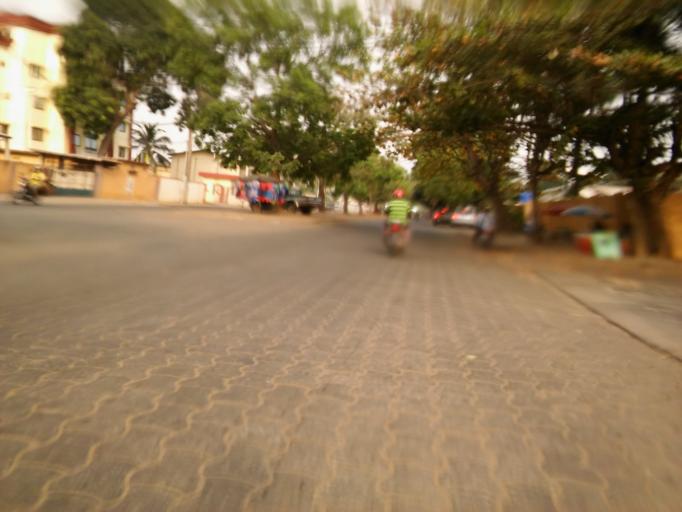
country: BJ
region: Littoral
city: Cotonou
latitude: 6.3566
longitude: 2.4019
